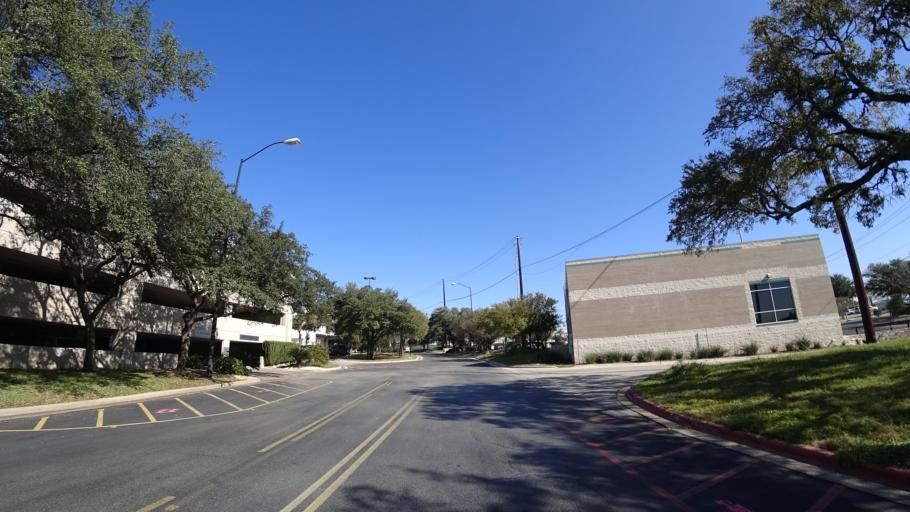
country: US
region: Texas
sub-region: Williamson County
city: Jollyville
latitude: 30.3898
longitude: -97.7474
